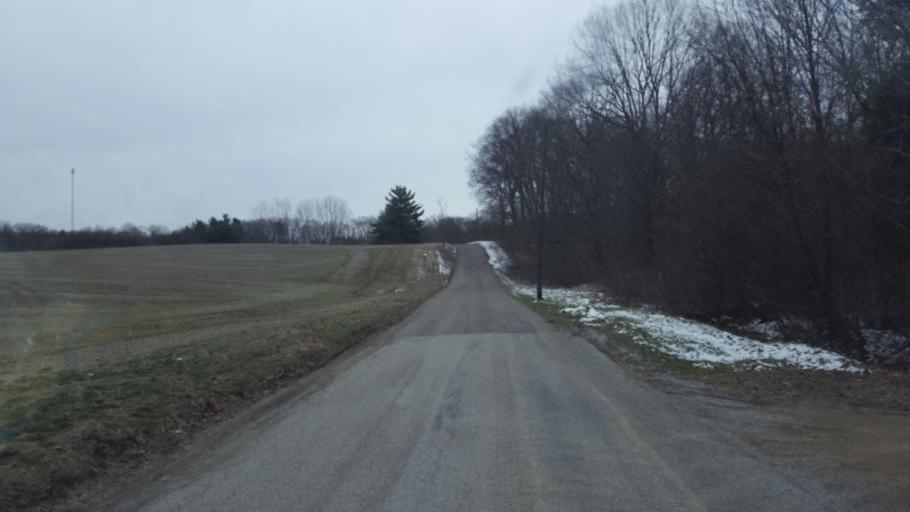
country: US
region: Ohio
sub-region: Sandusky County
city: Bellville
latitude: 40.5920
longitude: -82.4525
